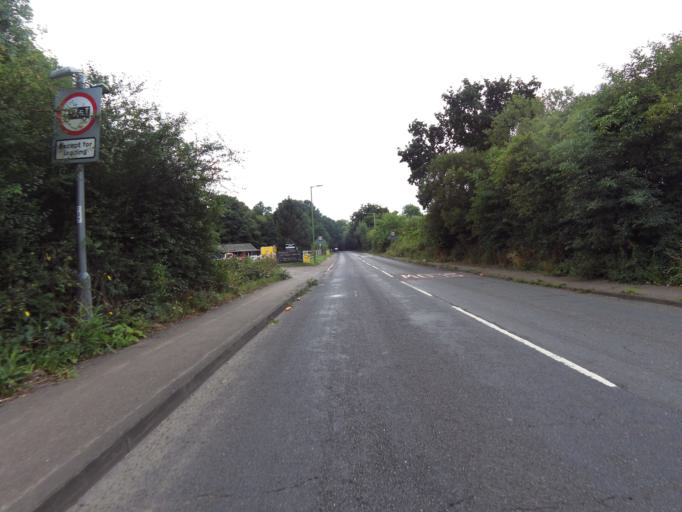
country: GB
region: England
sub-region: Hertfordshire
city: Shenley AV
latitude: 51.7167
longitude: -0.2998
